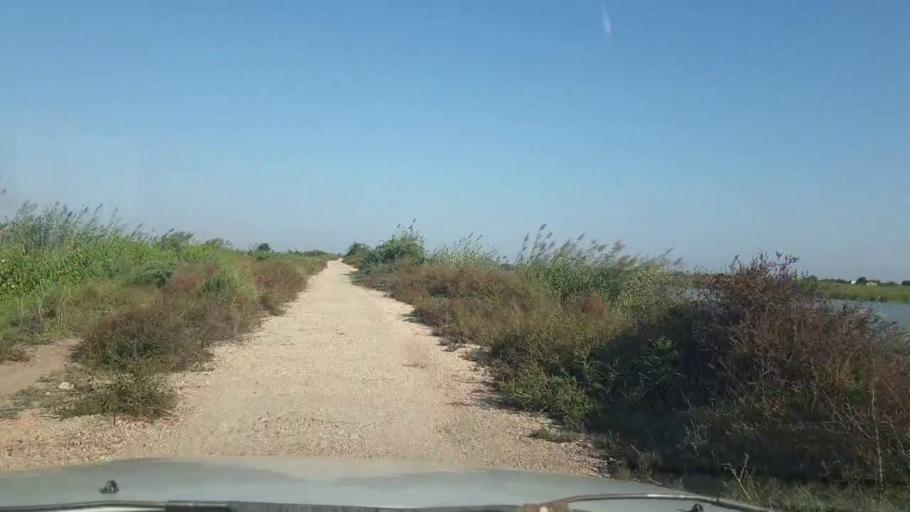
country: PK
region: Sindh
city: Chuhar Jamali
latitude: 24.5499
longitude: 67.9098
